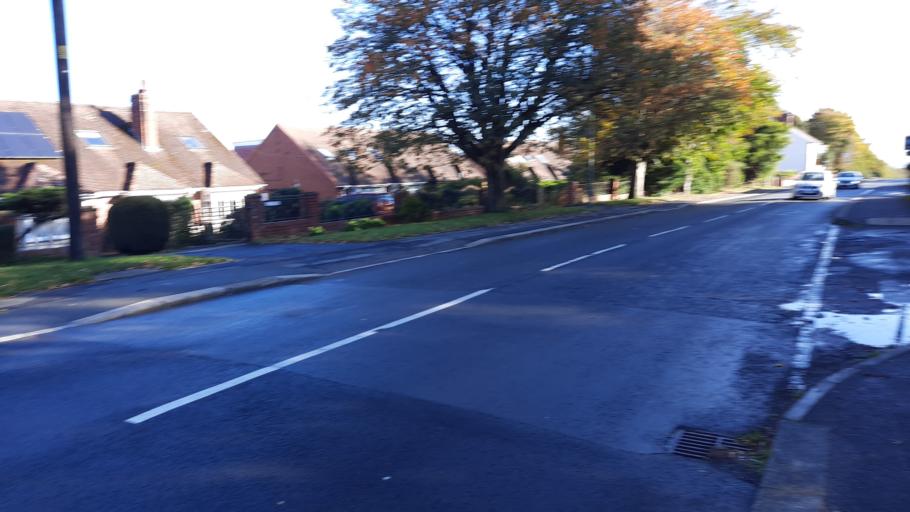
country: GB
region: England
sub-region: Sunderland
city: Ryhope
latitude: 54.8438
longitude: -1.3820
